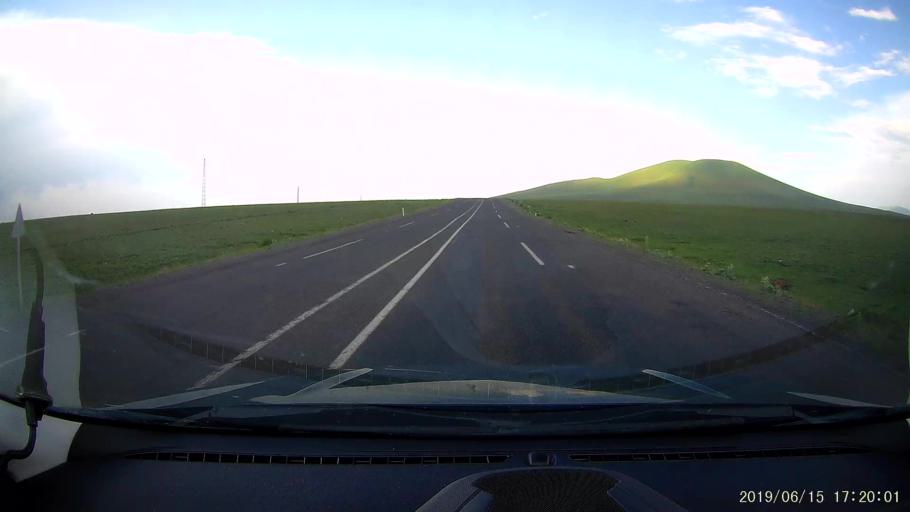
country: TR
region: Kars
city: Kars
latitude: 40.6160
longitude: 43.2916
